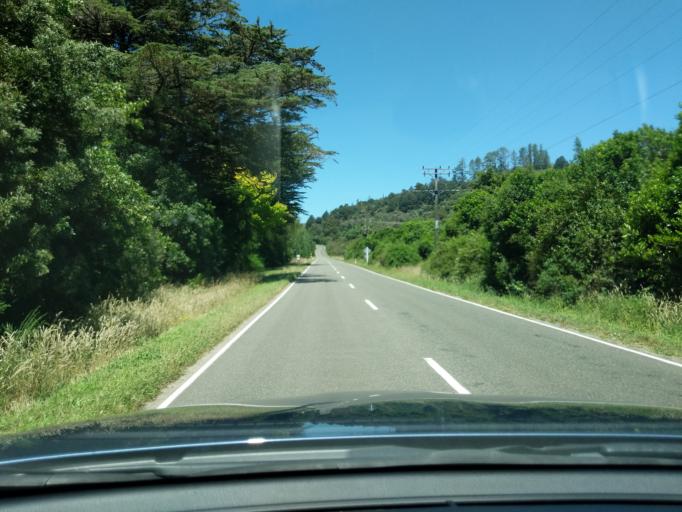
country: NZ
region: Tasman
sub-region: Tasman District
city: Takaka
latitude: -40.7222
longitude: 172.6001
